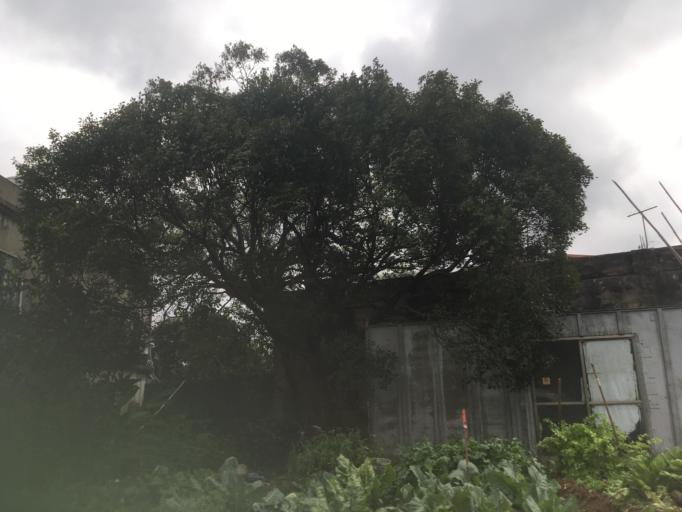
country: TW
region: Taiwan
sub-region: Miaoli
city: Miaoli
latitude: 24.4437
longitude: 120.7117
